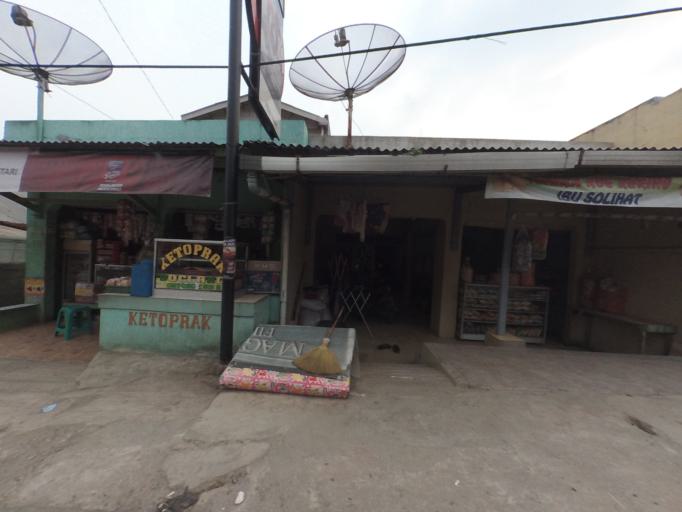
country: ID
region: West Java
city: Sidoger Lebak
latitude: -6.5663
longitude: 106.5949
